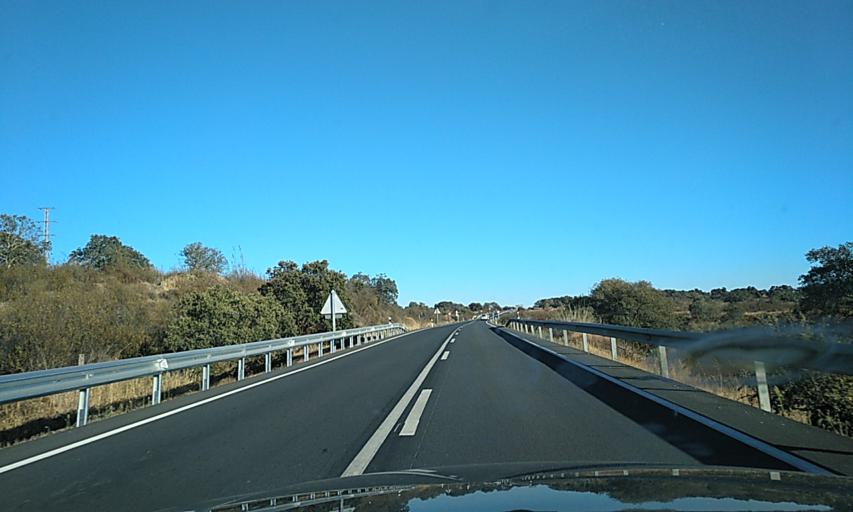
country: ES
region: Andalusia
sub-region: Provincia de Huelva
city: San Bartolome de la Torre
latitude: 37.4711
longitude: -7.1255
